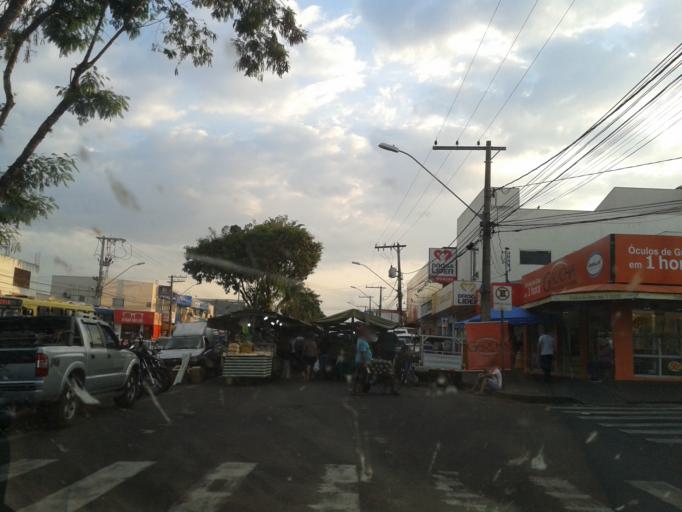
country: BR
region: Minas Gerais
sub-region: Uberlandia
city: Uberlandia
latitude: -18.9175
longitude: -48.3299
